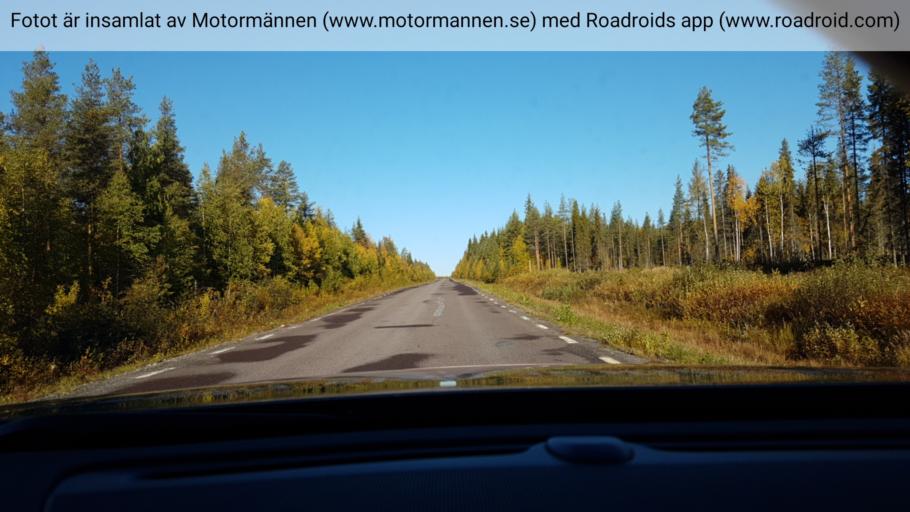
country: SE
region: Norrbotten
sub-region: Bodens Kommun
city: Boden
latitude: 66.0144
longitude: 21.5247
